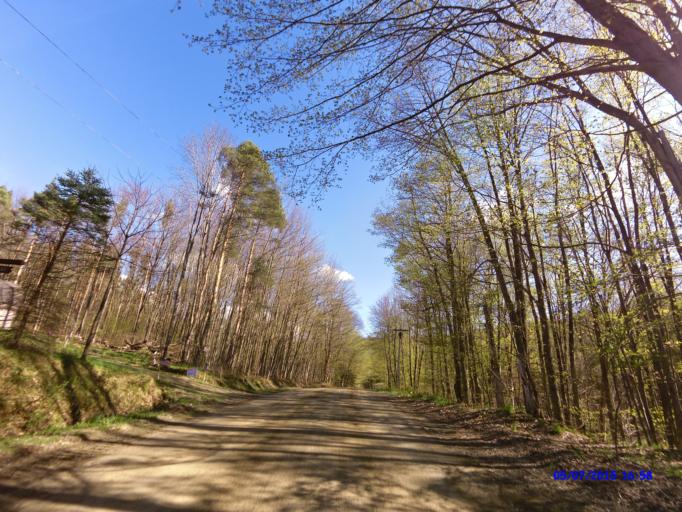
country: US
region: New York
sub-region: Cattaraugus County
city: Little Valley
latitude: 42.2956
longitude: -78.7469
